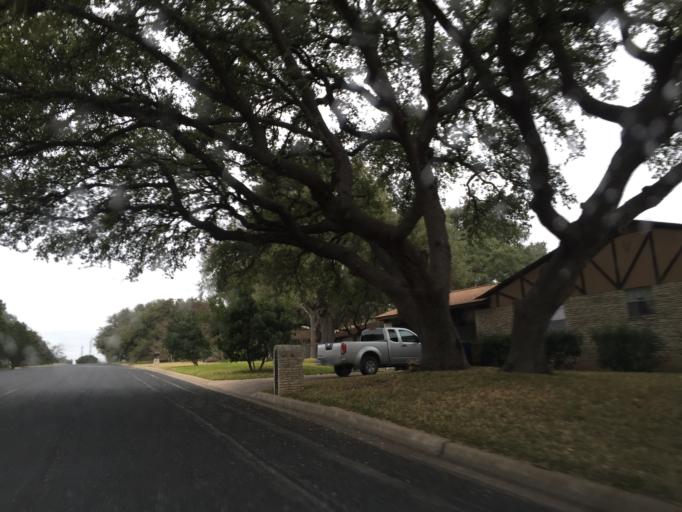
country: US
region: Texas
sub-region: Travis County
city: Wells Branch
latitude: 30.4049
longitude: -97.6831
